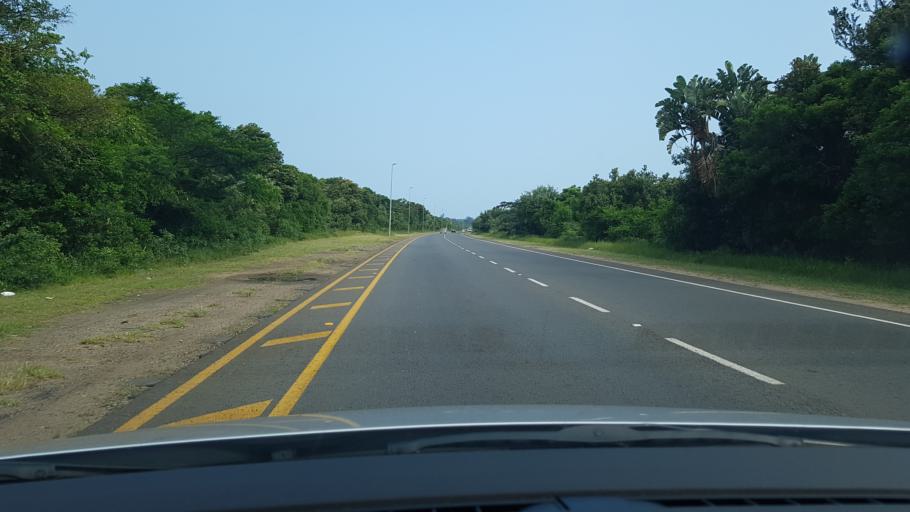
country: ZA
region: KwaZulu-Natal
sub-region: uThungulu District Municipality
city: Richards Bay
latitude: -28.7777
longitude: 32.0789
